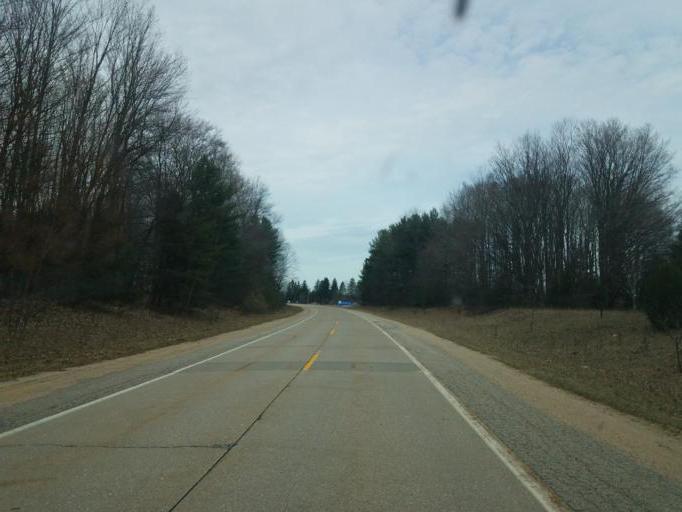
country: US
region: Michigan
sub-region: Oceana County
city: Hart
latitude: 43.7977
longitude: -86.3602
